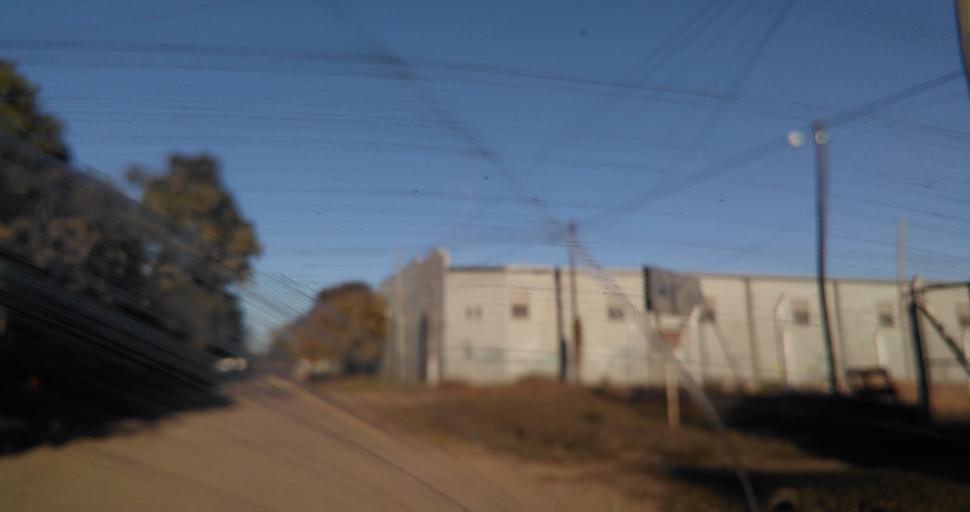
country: AR
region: Chaco
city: Fontana
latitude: -27.4350
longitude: -59.0167
